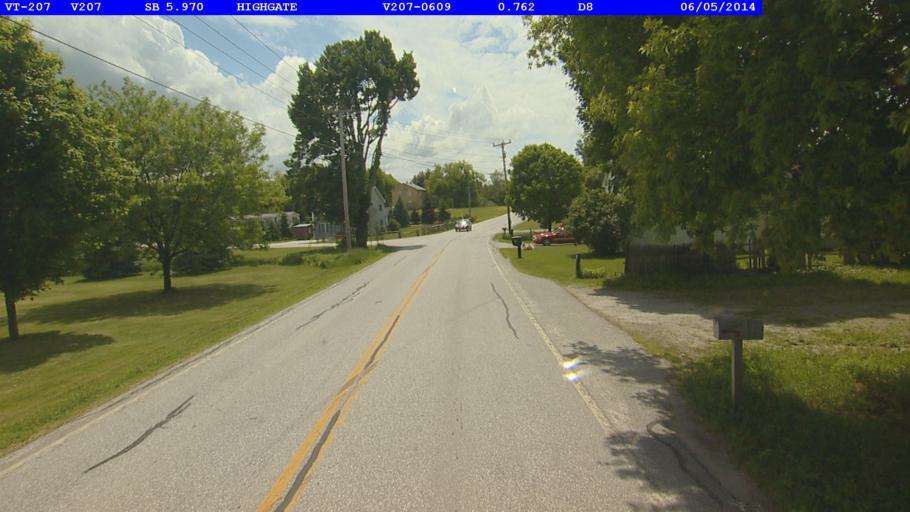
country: US
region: Vermont
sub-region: Franklin County
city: Swanton
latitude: 44.9218
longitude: -73.0530
